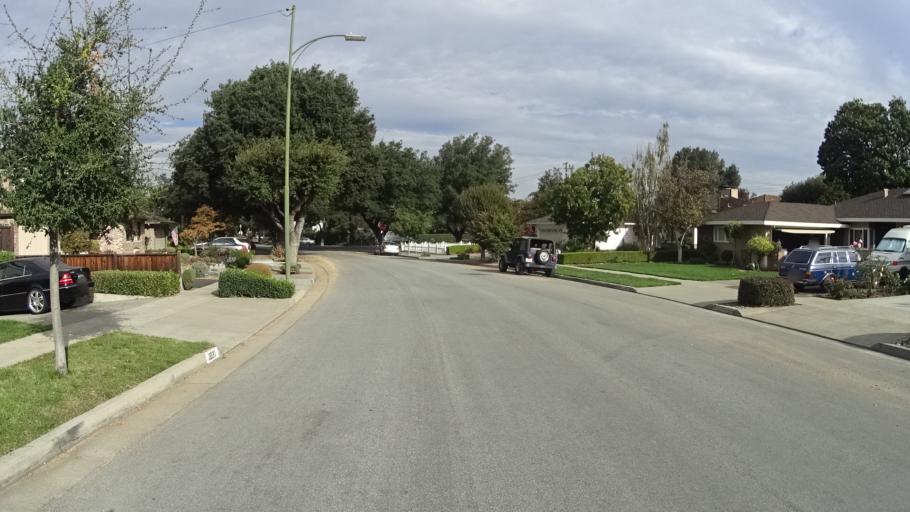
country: US
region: California
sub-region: Santa Clara County
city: Burbank
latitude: 37.3300
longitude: -121.9344
